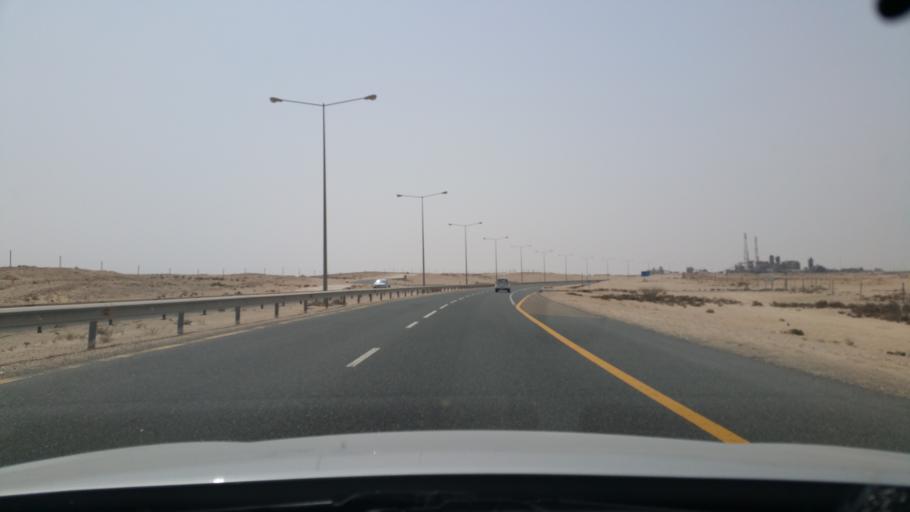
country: QA
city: Umm Bab
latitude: 25.2228
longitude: 50.8066
